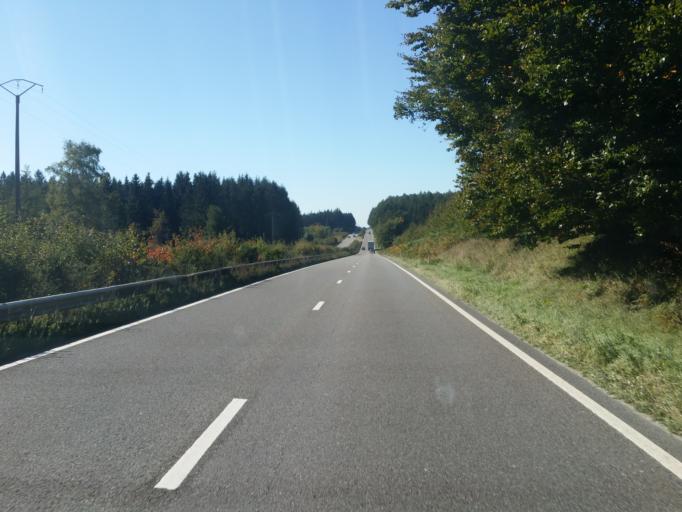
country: BE
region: Wallonia
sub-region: Province du Luxembourg
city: Bertrix
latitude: 49.8994
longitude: 5.3185
